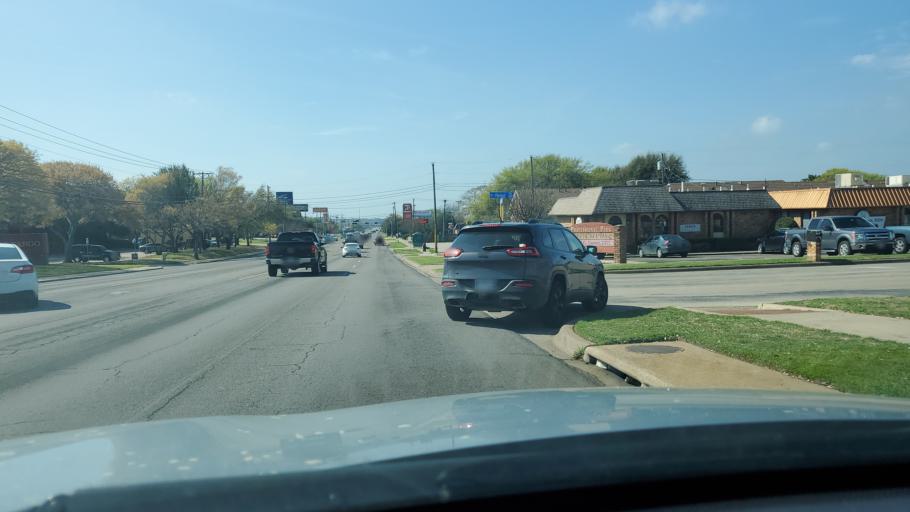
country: US
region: Texas
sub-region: Bell County
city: Temple
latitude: 31.0673
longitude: -97.3704
